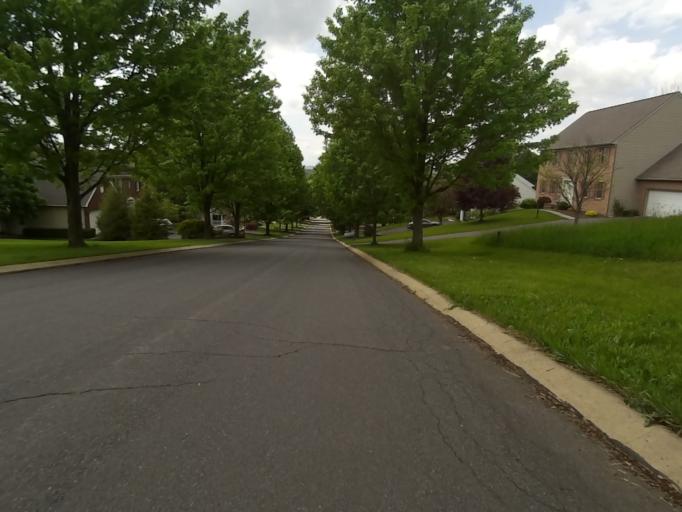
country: US
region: Pennsylvania
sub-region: Centre County
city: Lemont
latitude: 40.8074
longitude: -77.8142
